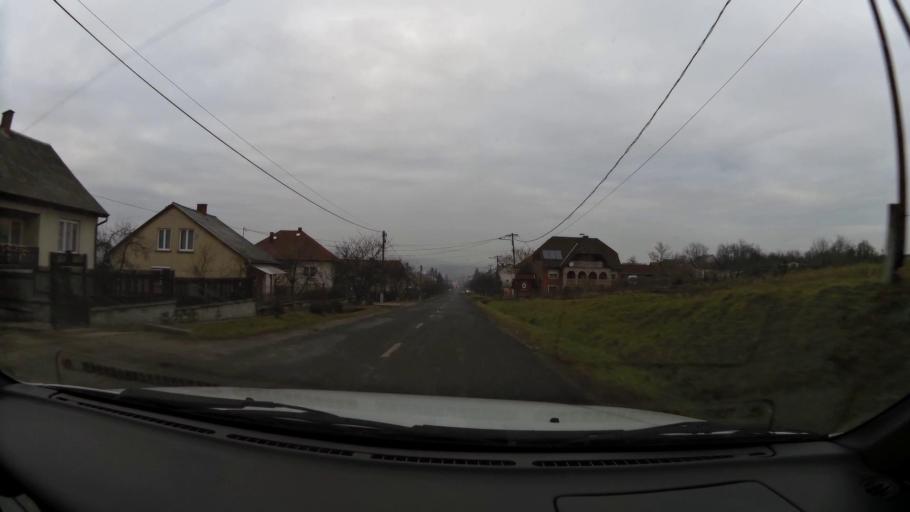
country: HU
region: Borsod-Abauj-Zemplen
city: Rudabanya
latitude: 48.4020
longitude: 20.6311
